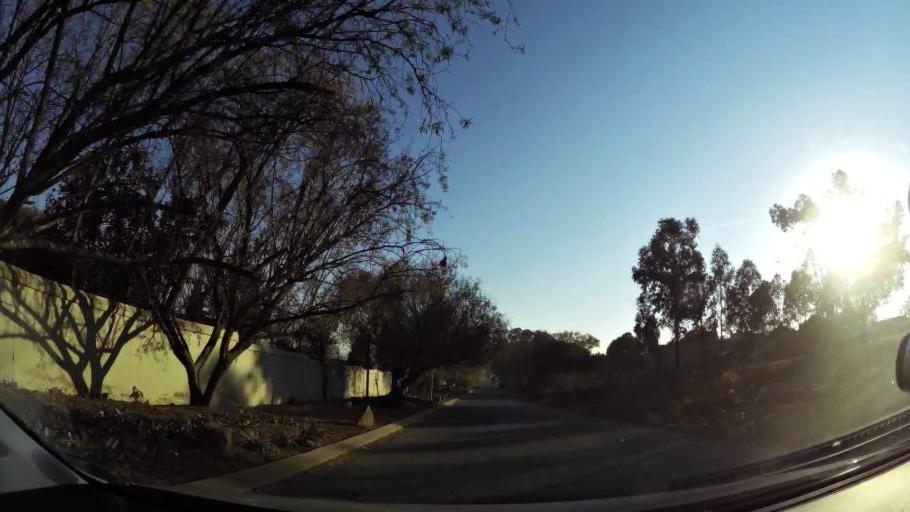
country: ZA
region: Gauteng
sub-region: City of Johannesburg Metropolitan Municipality
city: Midrand
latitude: -26.0489
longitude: 28.1106
